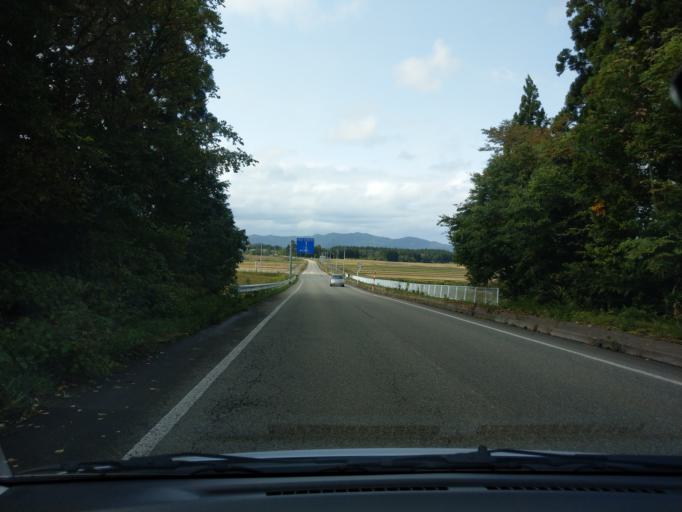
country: JP
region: Akita
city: Omagari
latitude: 39.5243
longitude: 140.2891
